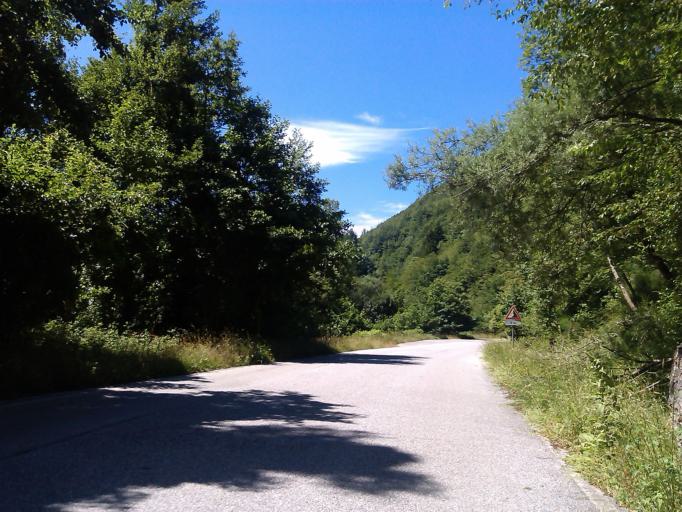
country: IT
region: Tuscany
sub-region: Provincia di Prato
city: Cantagallo
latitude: 44.0706
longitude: 11.0539
